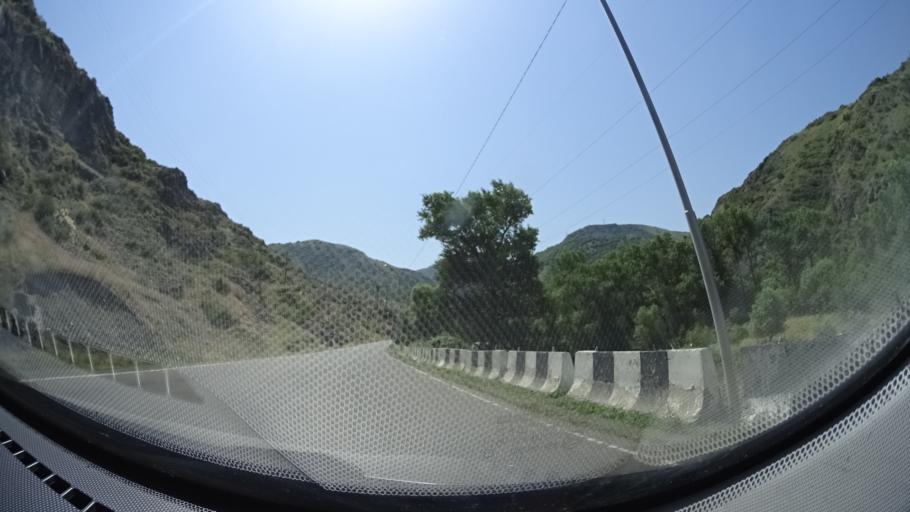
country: GE
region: Samtskhe-Javakheti
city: Aspindza
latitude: 41.5633
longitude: 43.2696
